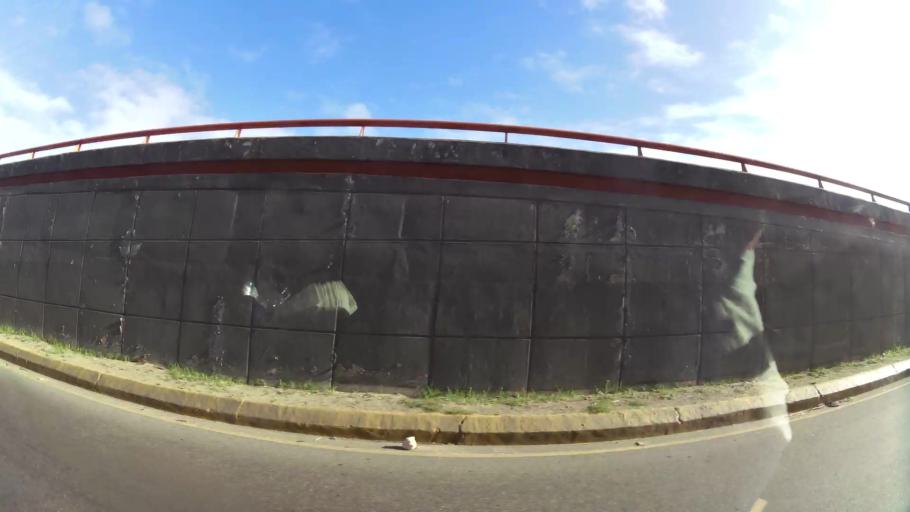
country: DO
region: Nacional
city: La Agustina
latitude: 18.4842
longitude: -69.9390
